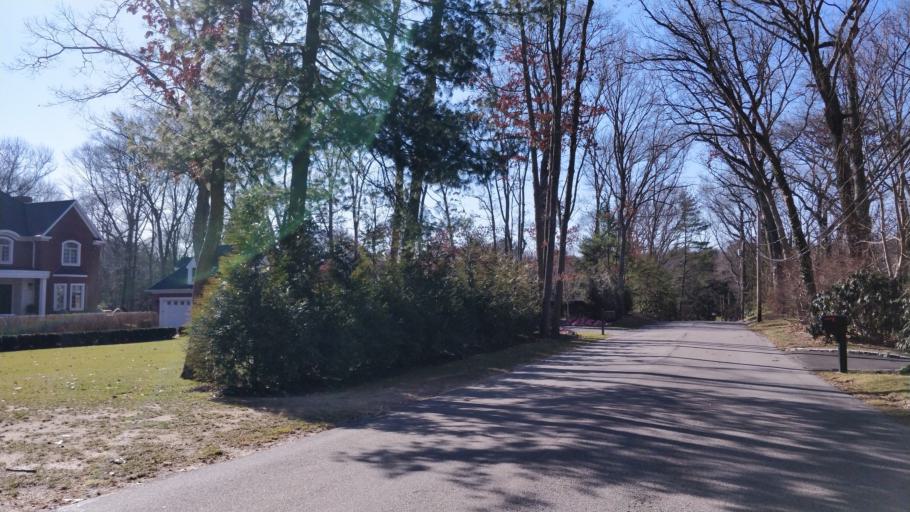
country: US
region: New York
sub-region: Nassau County
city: Upper Brookville
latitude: 40.8507
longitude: -73.5587
